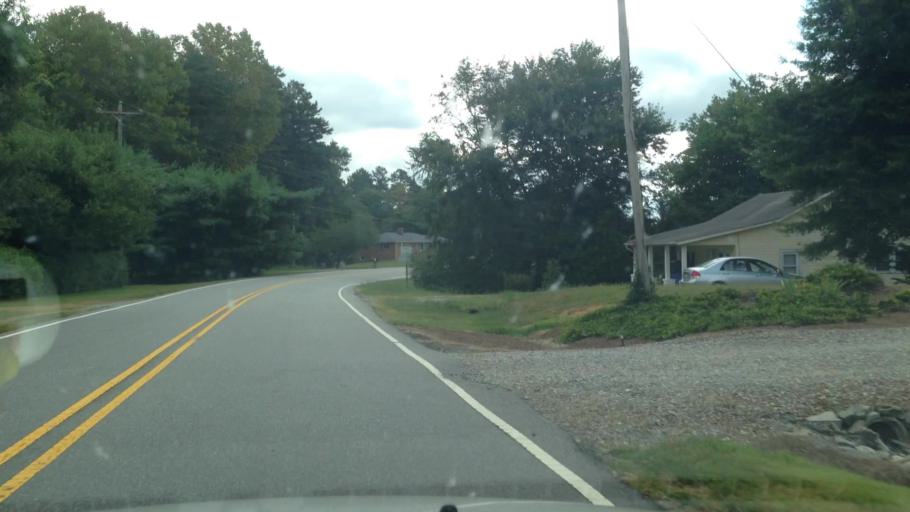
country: US
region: North Carolina
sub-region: Rockingham County
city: Mayodan
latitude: 36.3994
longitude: -80.0343
